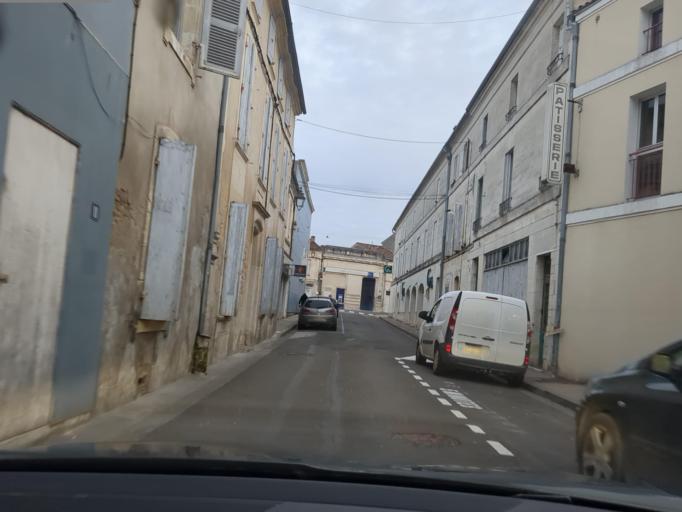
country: FR
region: Poitou-Charentes
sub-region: Departement de la Charente-Maritime
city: Jonzac
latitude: 45.4447
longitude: -0.4348
